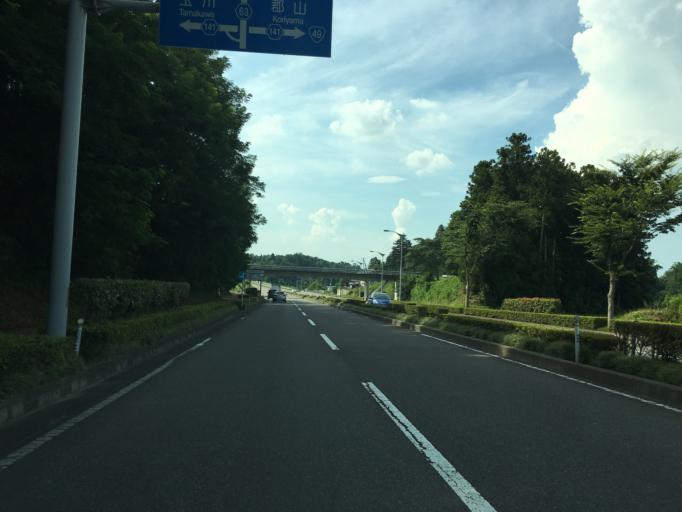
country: JP
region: Fukushima
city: Sukagawa
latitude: 37.2605
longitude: 140.4196
